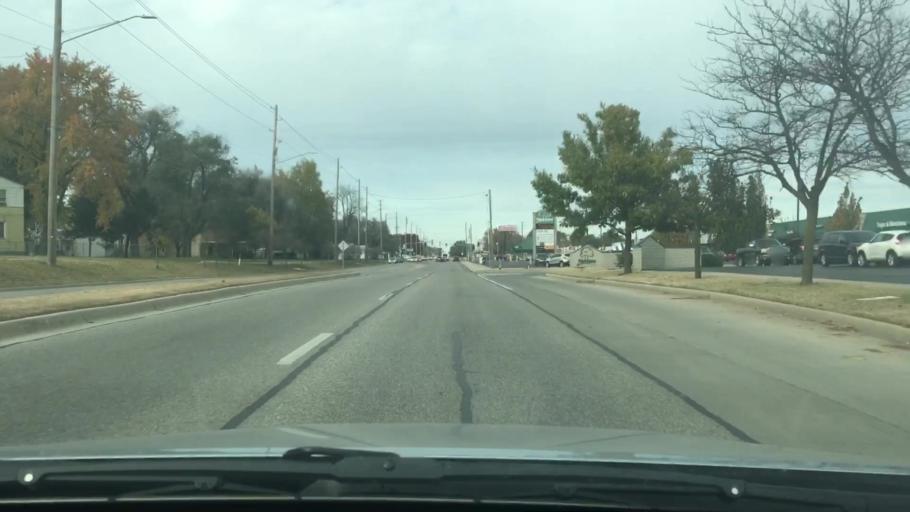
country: US
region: Kansas
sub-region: Sedgwick County
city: Wichita
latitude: 37.6689
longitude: -97.2804
